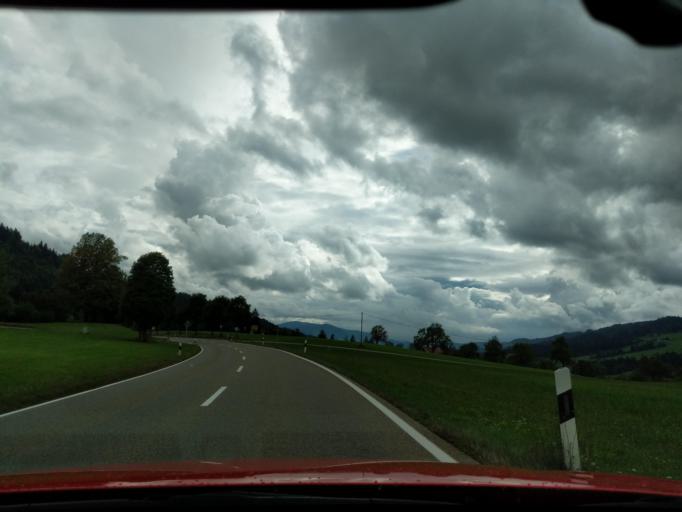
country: AT
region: Vorarlberg
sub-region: Politischer Bezirk Bregenz
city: Riefensberg
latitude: 47.5294
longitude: 9.9816
